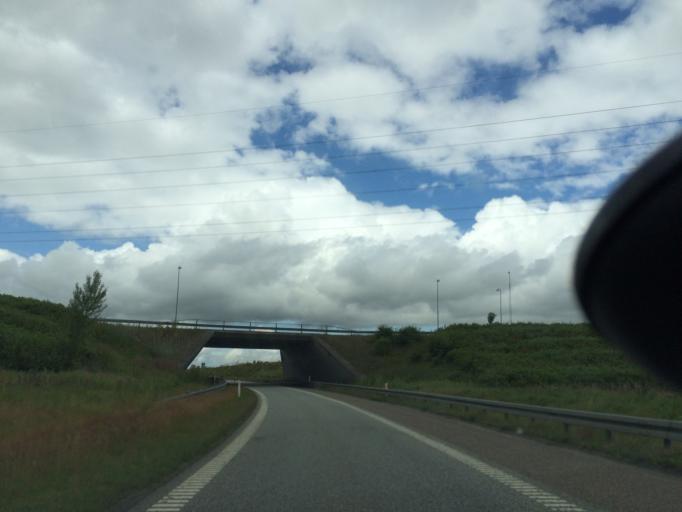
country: DK
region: Central Jutland
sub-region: Arhus Kommune
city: Kolt
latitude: 56.1567
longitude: 10.0699
